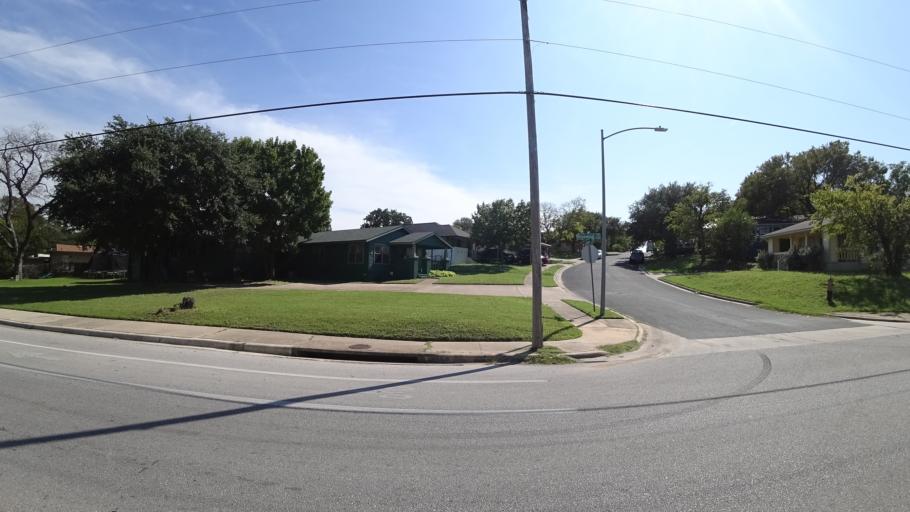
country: US
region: Texas
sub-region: Travis County
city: Austin
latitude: 30.2693
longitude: -97.7220
